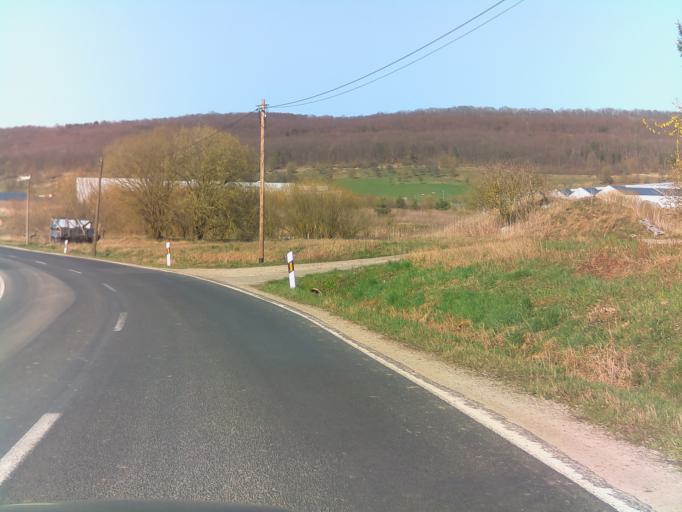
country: DE
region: Thuringia
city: Wolfershausen
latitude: 50.4377
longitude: 10.4606
